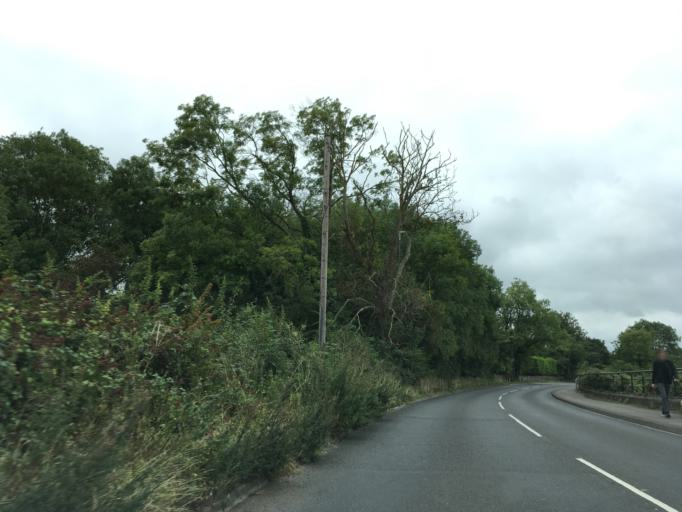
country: GB
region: England
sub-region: Bath and North East Somerset
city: Keynsham
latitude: 51.4221
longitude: -2.4879
